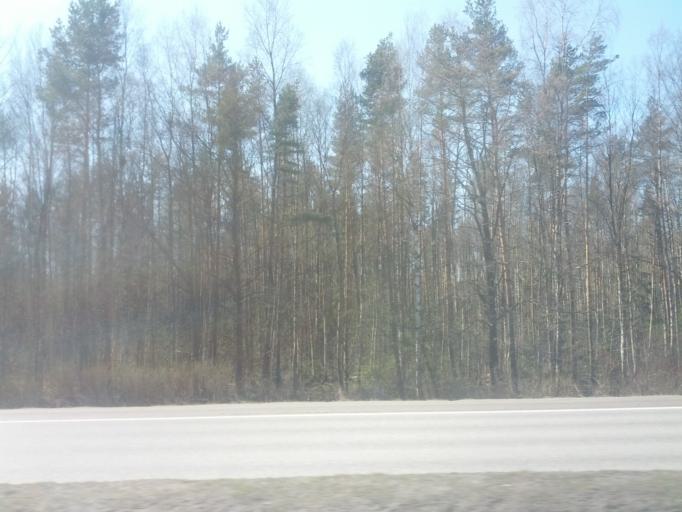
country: RU
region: St.-Petersburg
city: Razliv
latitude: 60.0739
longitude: 29.9664
